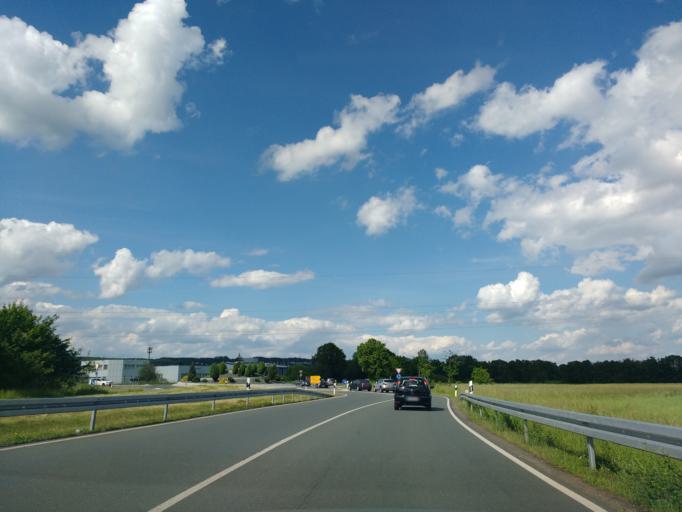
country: DE
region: Hesse
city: Allendorf
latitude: 51.0194
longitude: 8.6677
